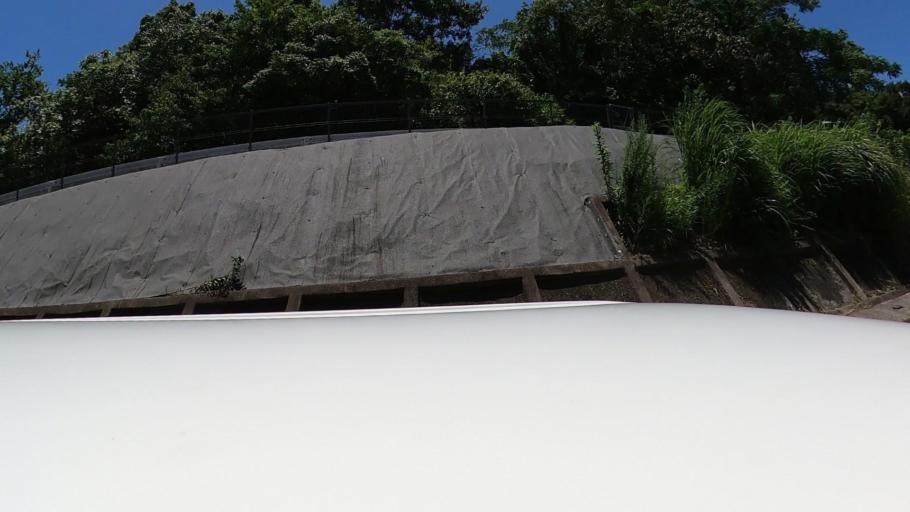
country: JP
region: Miyazaki
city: Nobeoka
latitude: 32.4049
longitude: 131.6141
